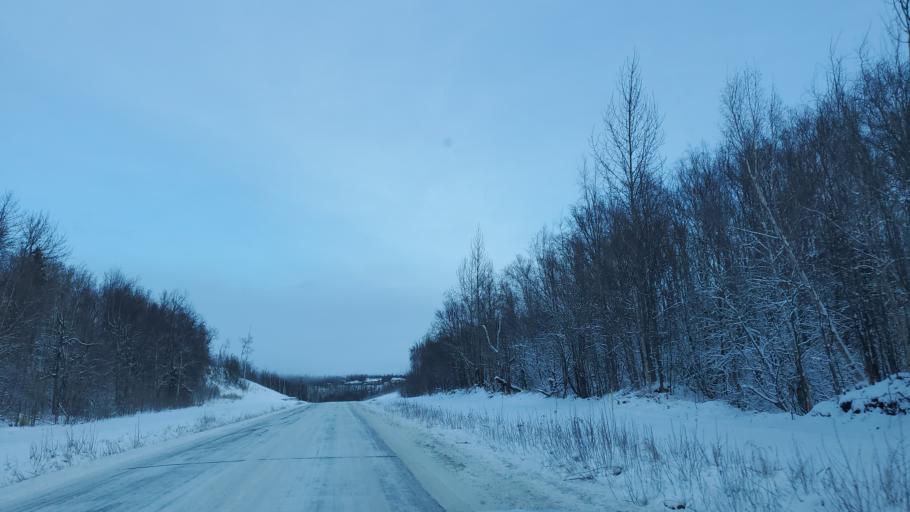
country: US
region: Alaska
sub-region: Matanuska-Susitna Borough
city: Lakes
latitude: 61.5489
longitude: -149.3081
